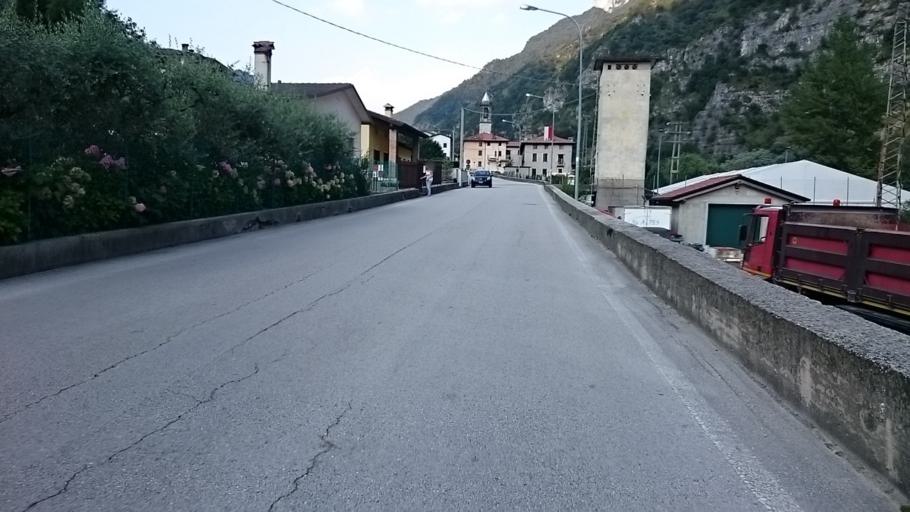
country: IT
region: Veneto
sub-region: Provincia di Vicenza
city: Valstagna
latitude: 45.8735
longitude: 11.6733
